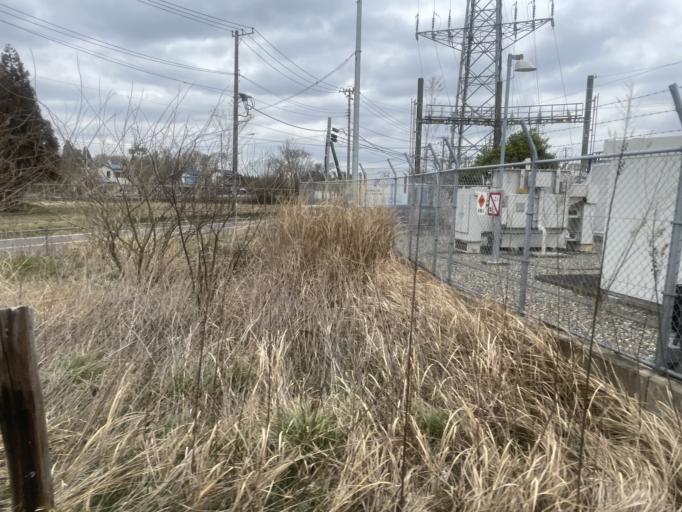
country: JP
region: Chiba
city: Chiba
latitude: 35.5545
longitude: 140.1946
